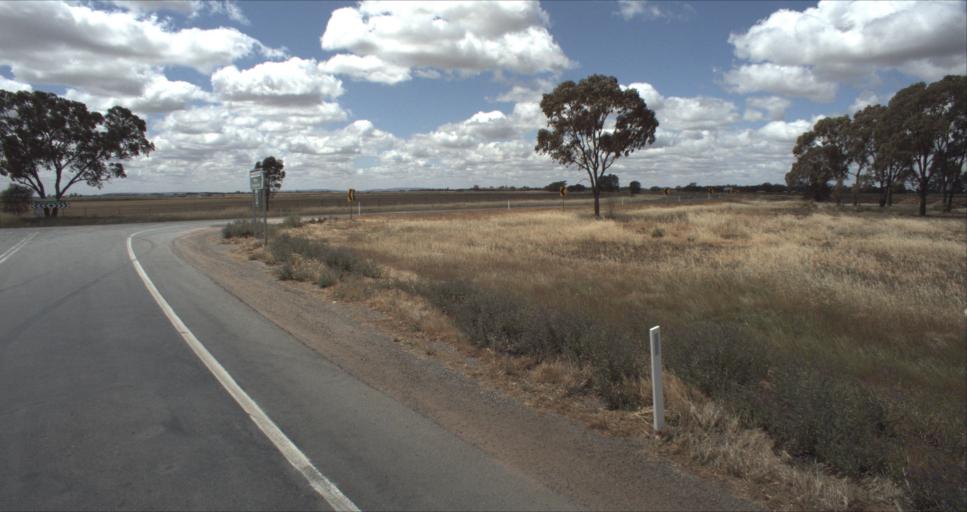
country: AU
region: New South Wales
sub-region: Murrumbidgee Shire
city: Darlington Point
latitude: -34.5033
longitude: 146.1880
